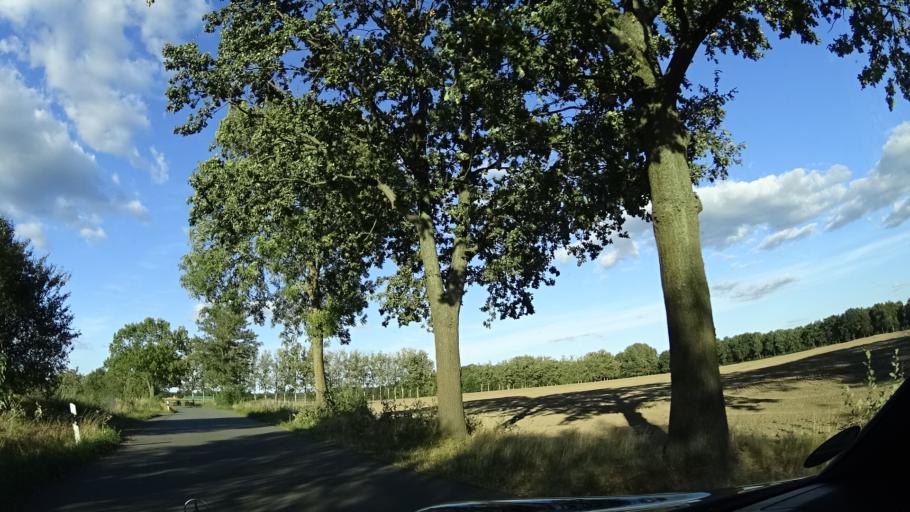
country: DE
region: Brandenburg
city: Neuruppin
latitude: 52.9529
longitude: 12.7611
